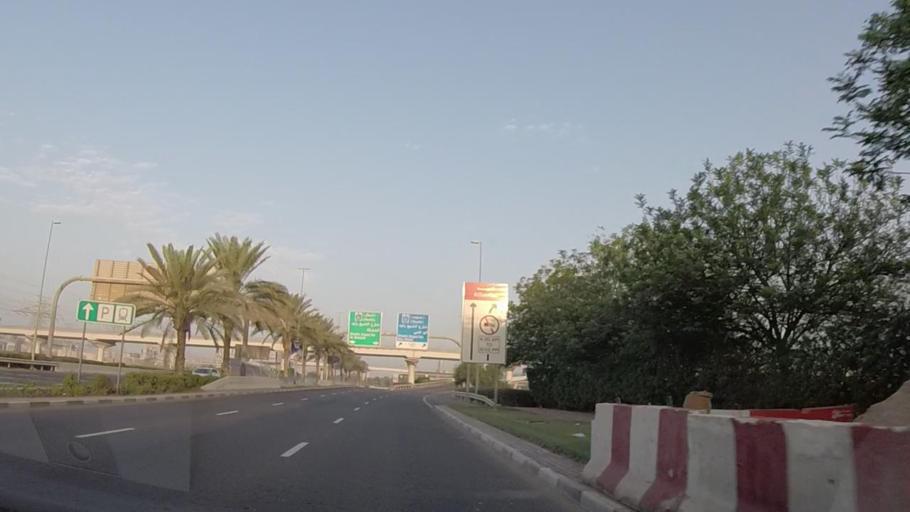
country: AE
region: Dubai
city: Dubai
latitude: 25.0524
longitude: 55.1256
